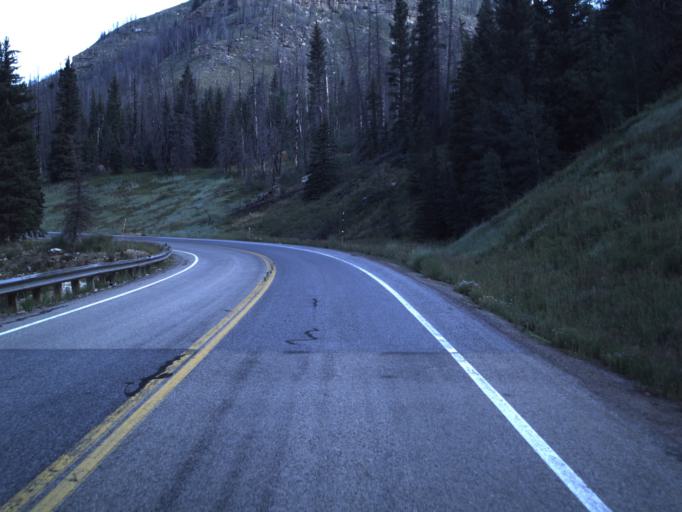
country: US
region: Utah
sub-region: Emery County
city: Huntington
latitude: 39.5358
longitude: -111.1563
